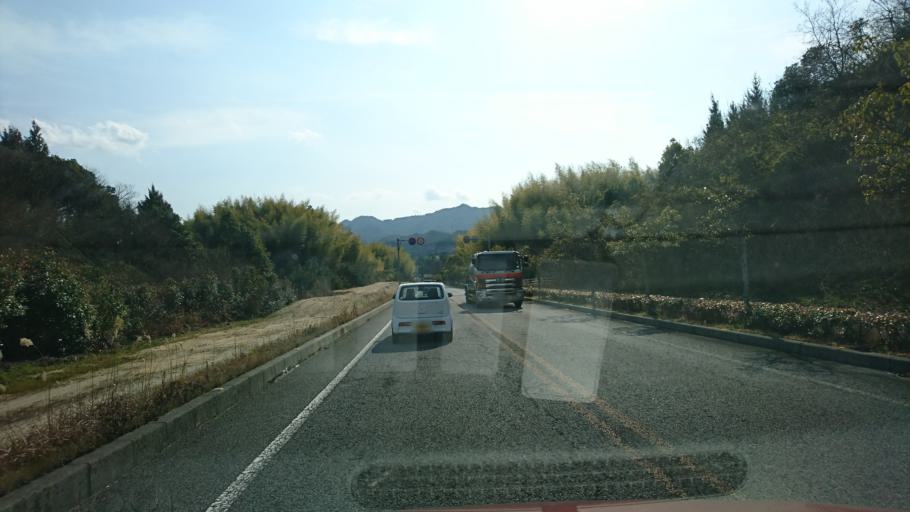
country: JP
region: Ehime
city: Saijo
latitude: 34.0095
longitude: 133.0339
